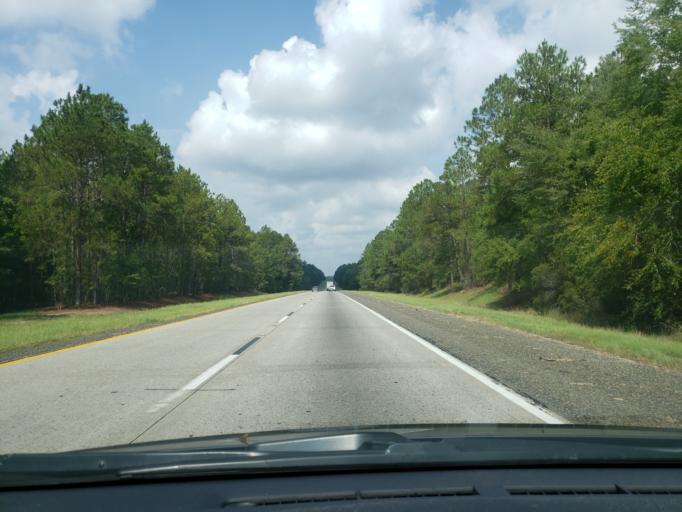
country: US
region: Georgia
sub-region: Treutlen County
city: Soperton
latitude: 32.4344
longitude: -82.6313
